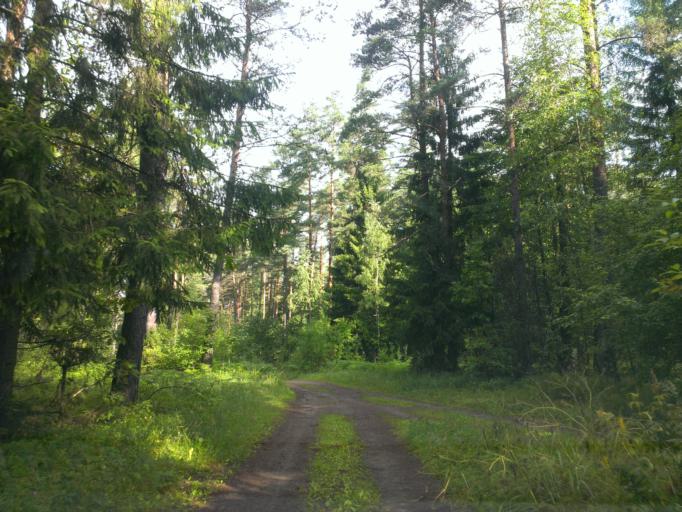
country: LV
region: Incukalns
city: Vangazi
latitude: 57.1008
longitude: 24.5362
